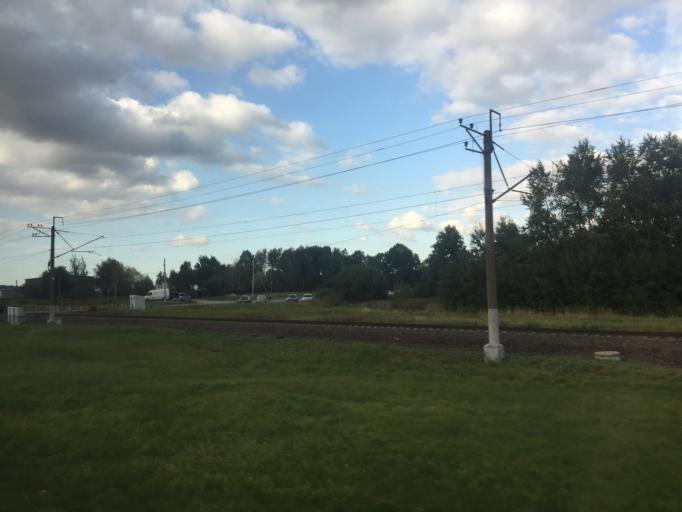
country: RU
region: Kaliningrad
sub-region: Gorod Kaliningrad
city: Kaliningrad
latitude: 54.7684
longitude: 20.4287
